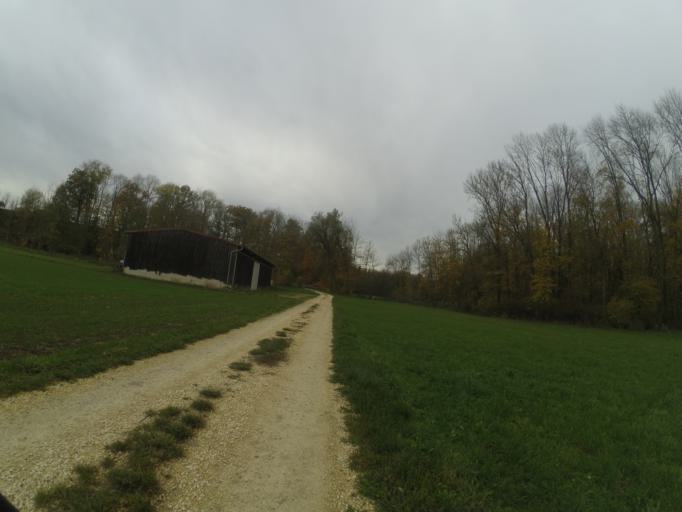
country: DE
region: Bavaria
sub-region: Swabia
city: Senden
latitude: 48.3434
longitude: 10.0039
